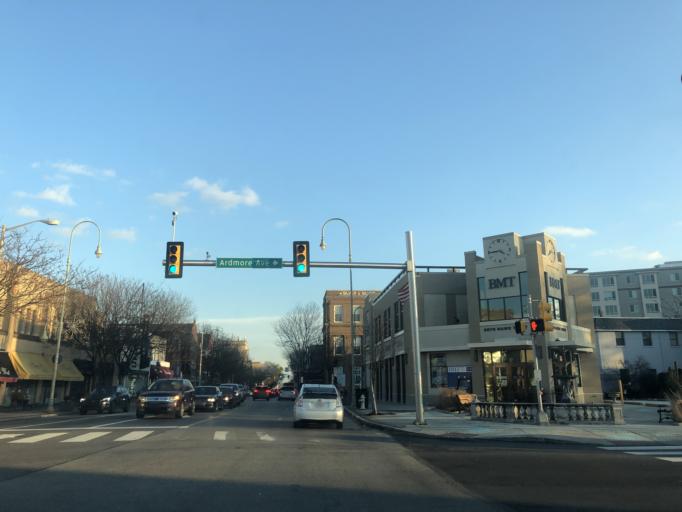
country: US
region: Pennsylvania
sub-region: Montgomery County
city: Ardmore
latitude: 40.0090
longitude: -75.2934
